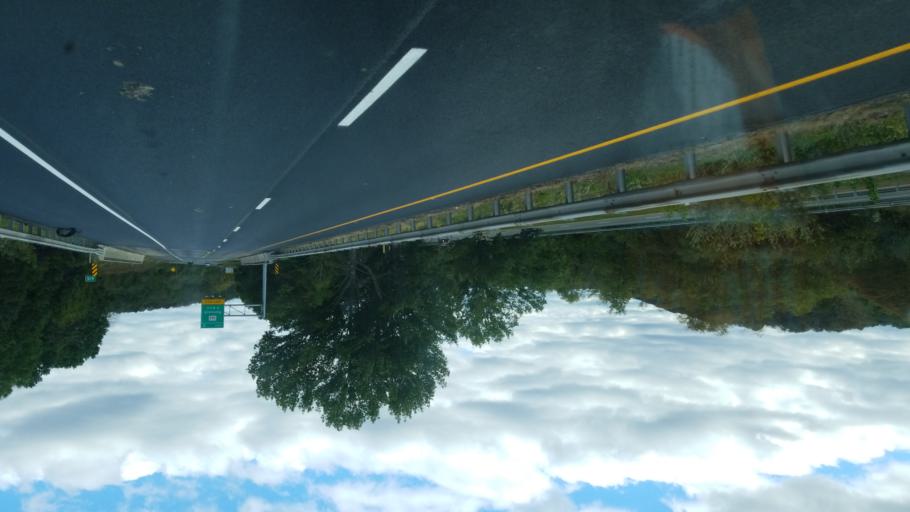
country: US
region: Maryland
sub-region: Washington County
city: Hancock
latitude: 39.6900
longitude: -78.1276
